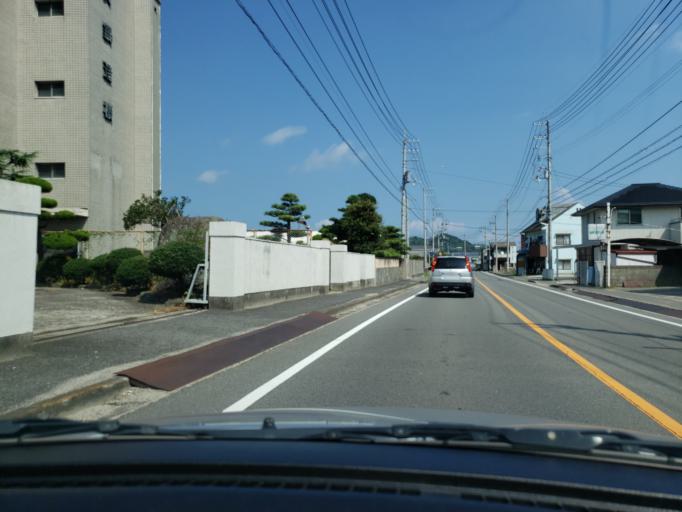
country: JP
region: Ehime
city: Hojo
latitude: 34.0963
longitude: 132.9732
